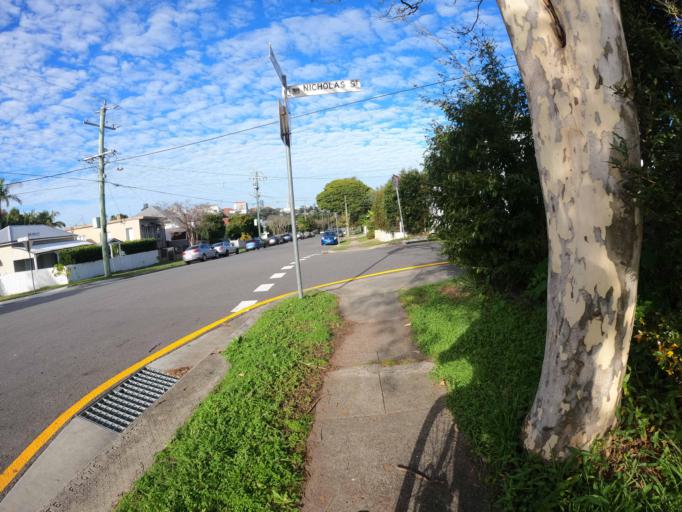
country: AU
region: Queensland
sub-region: Brisbane
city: Windsor
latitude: -27.4402
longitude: 153.0270
